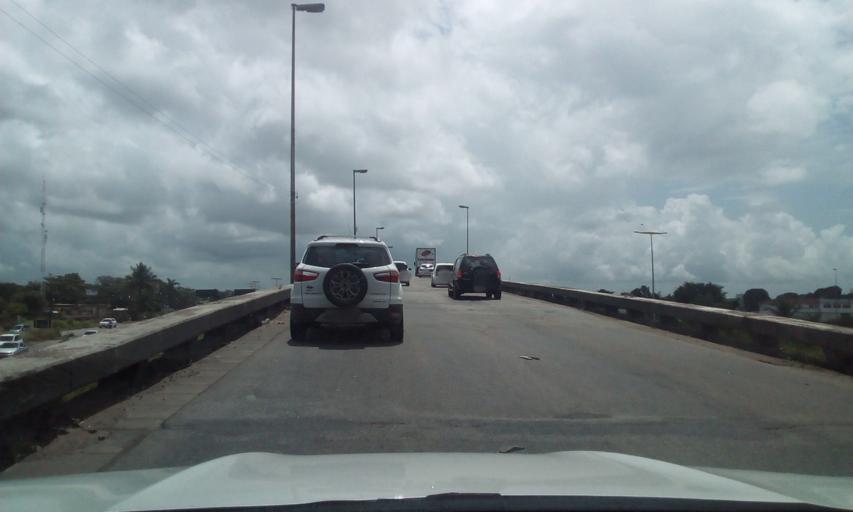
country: BR
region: Pernambuco
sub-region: Recife
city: Recife
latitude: -8.0658
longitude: -34.9436
